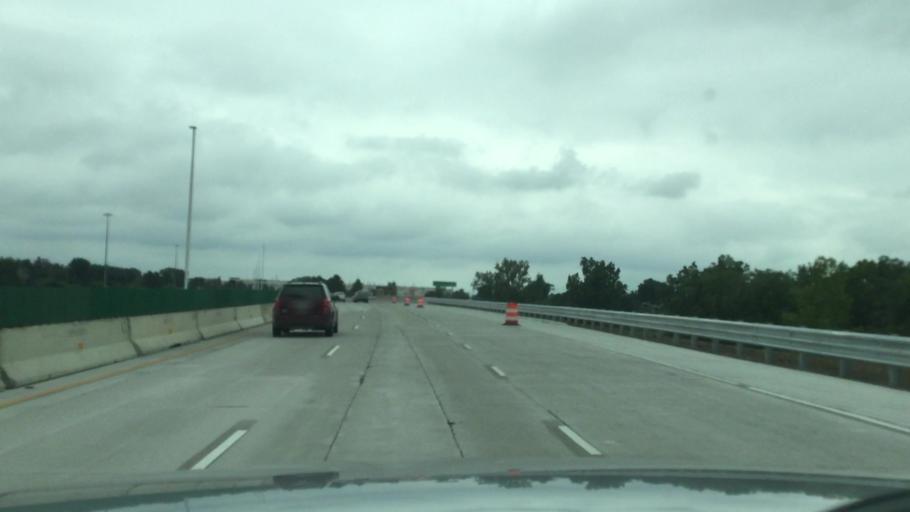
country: US
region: Michigan
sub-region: Genesee County
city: Flint
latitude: 42.9984
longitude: -83.7049
